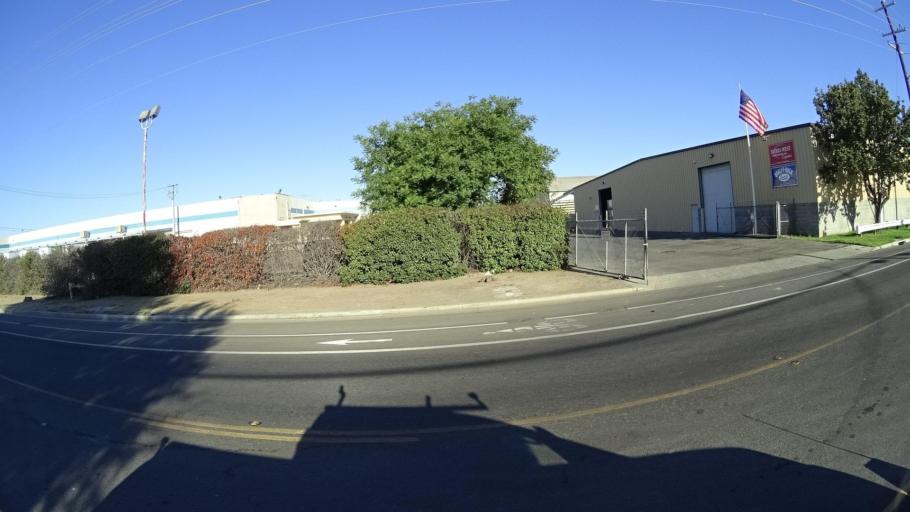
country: US
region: California
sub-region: Fresno County
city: Fresno
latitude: 36.7109
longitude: -119.7637
